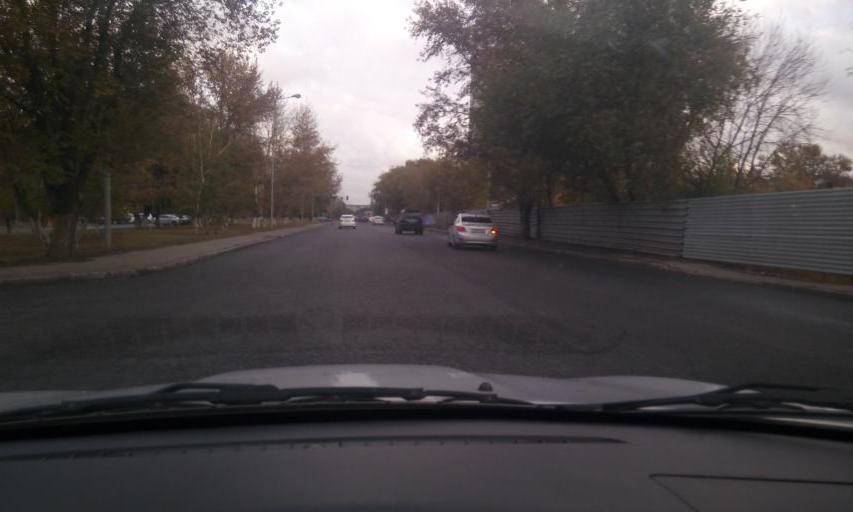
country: KZ
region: Astana Qalasy
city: Astana
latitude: 51.1660
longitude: 71.4639
